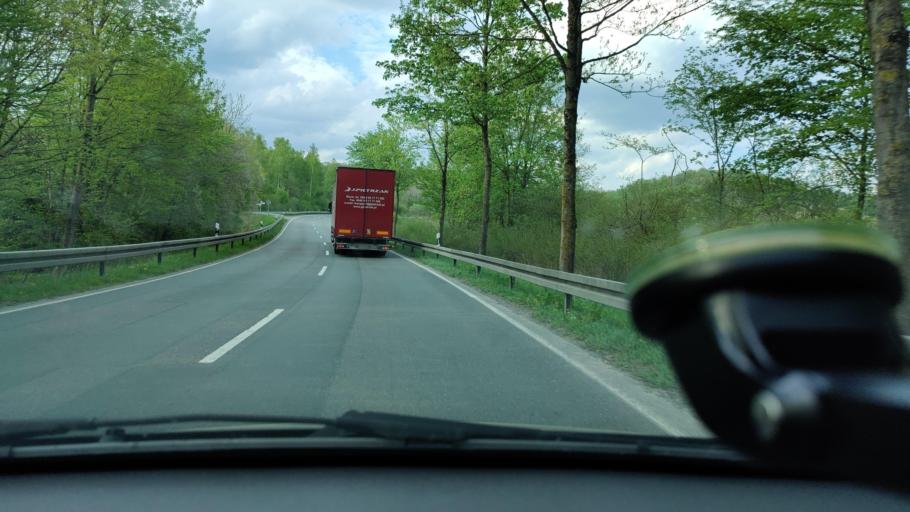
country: DE
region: North Rhine-Westphalia
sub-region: Regierungsbezirk Detmold
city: Wunnenberg
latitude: 51.4811
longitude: 8.6559
